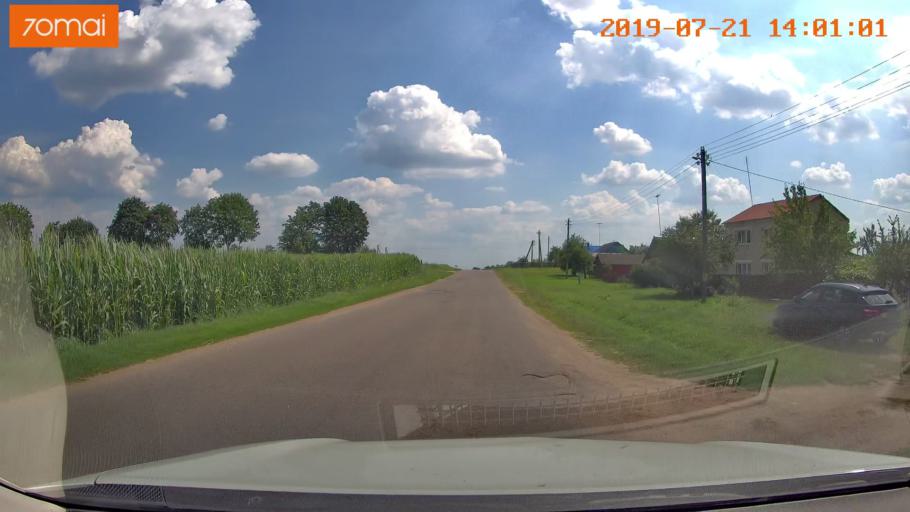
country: BY
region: Grodnenskaya
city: Lyubcha
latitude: 53.7474
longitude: 26.0704
